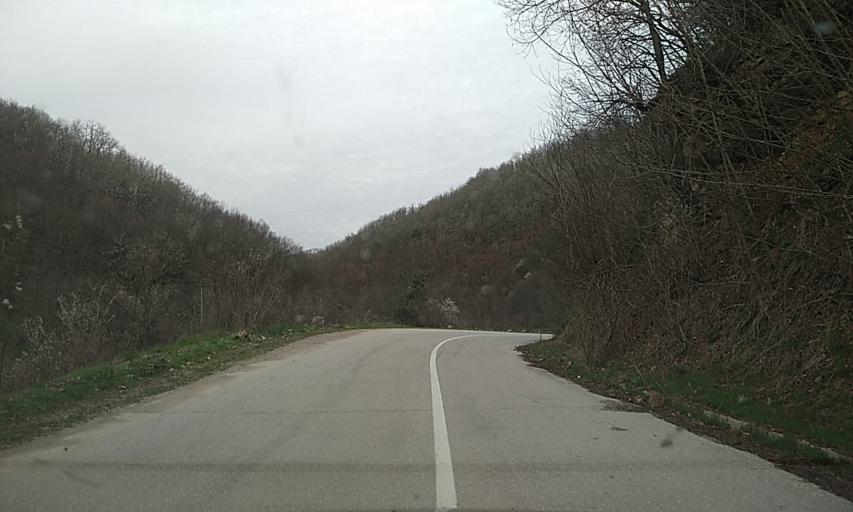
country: RS
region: Central Serbia
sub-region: Pcinjski Okrug
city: Bosilegrad
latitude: 42.4174
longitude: 22.5161
